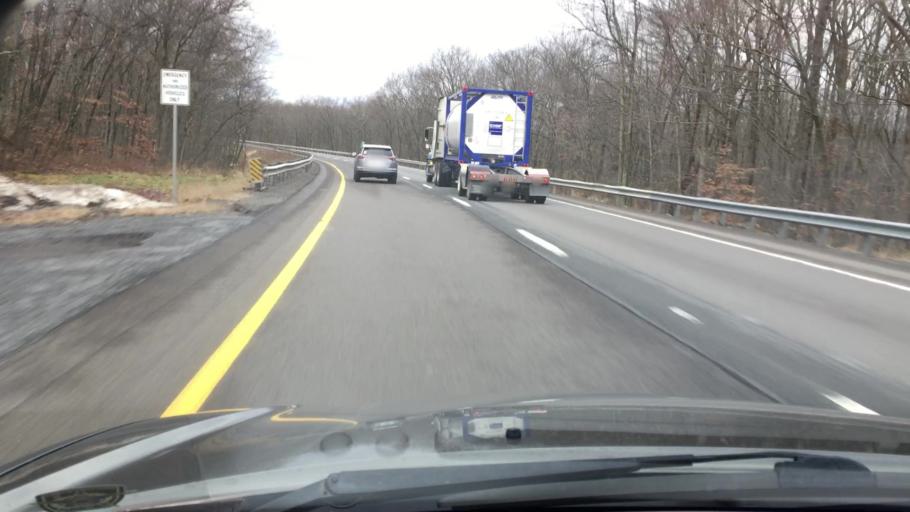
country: US
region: Pennsylvania
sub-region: Carbon County
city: Towamensing Trails
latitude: 41.0834
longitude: -75.6229
